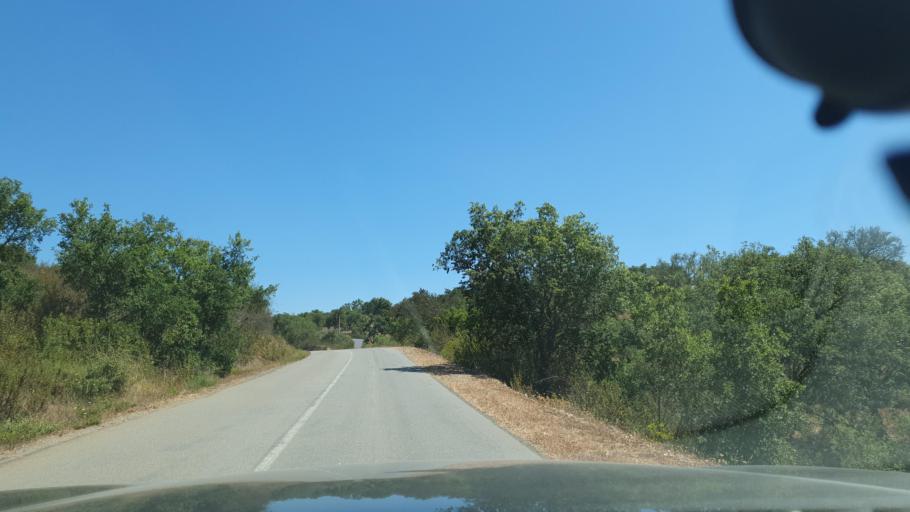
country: PT
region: Beja
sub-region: Odemira
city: Odemira
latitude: 37.5372
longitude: -8.4653
